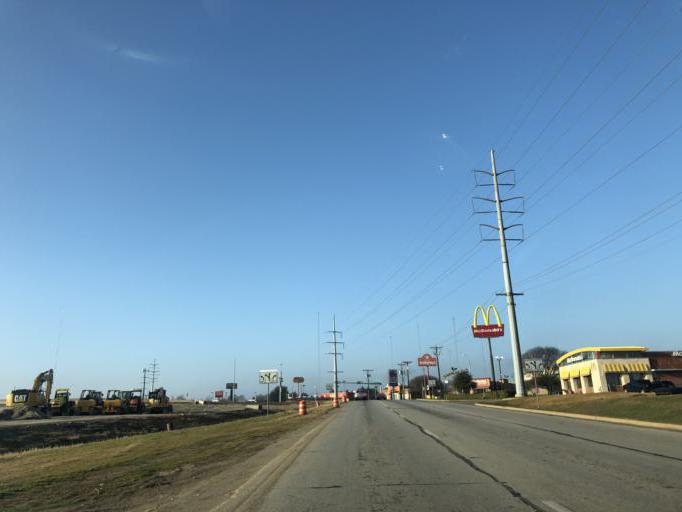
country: US
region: Texas
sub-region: Dallas County
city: Cedar Hill
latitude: 32.5972
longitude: -96.9393
